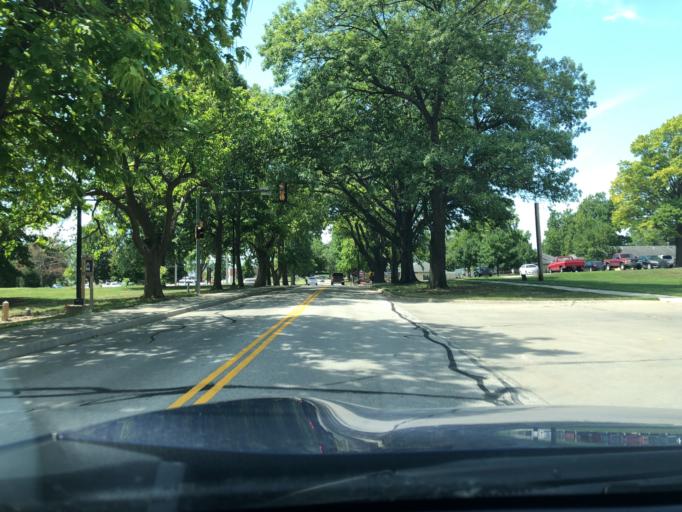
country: US
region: Kansas
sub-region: Leavenworth County
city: Leavenworth
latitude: 39.3486
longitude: -94.9295
